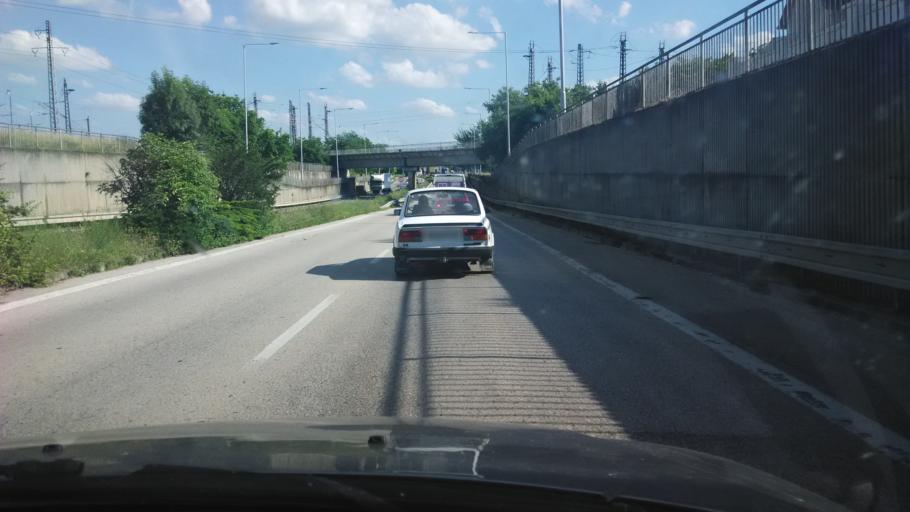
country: SK
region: Nitriansky
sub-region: Okres Nove Zamky
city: Nove Zamky
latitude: 48.0065
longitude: 18.1565
